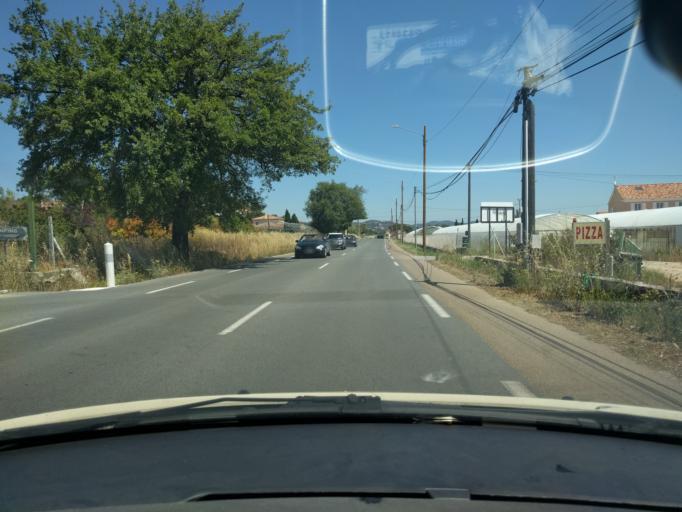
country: FR
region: Provence-Alpes-Cote d'Azur
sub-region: Departement du Var
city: Hyeres
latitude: 43.0893
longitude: 6.1289
